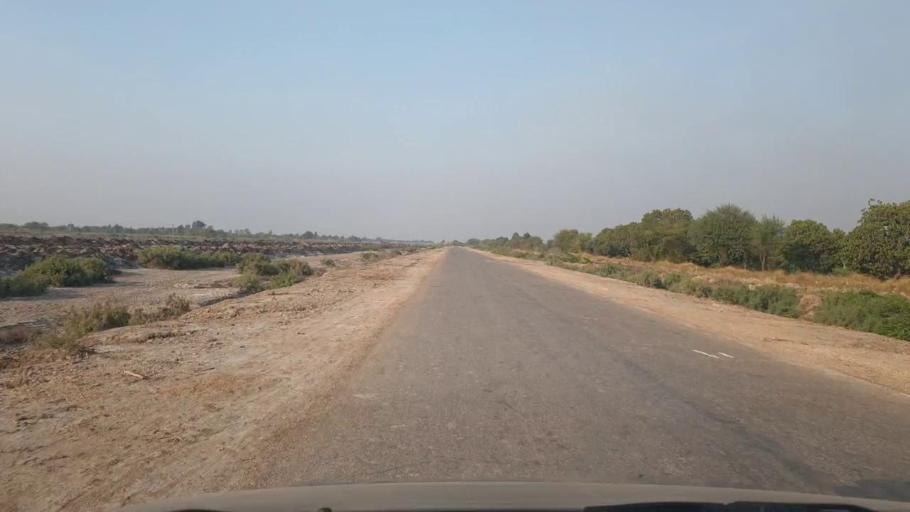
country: PK
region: Sindh
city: Mirwah Gorchani
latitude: 25.3591
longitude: 69.1752
